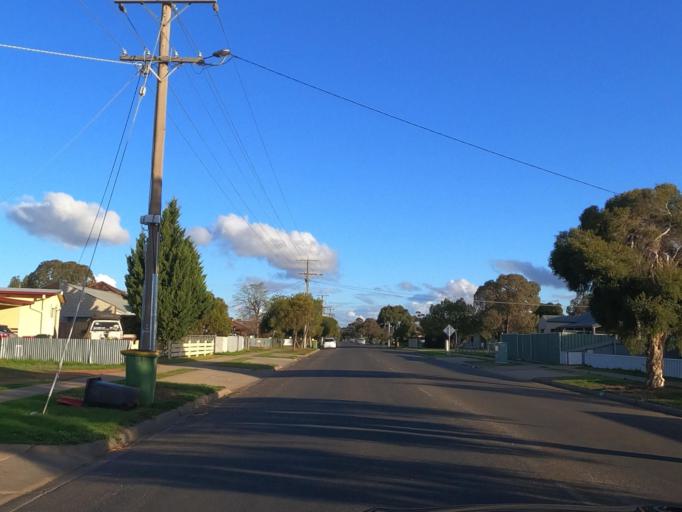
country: AU
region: Victoria
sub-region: Swan Hill
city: Swan Hill
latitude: -35.3409
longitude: 143.5441
